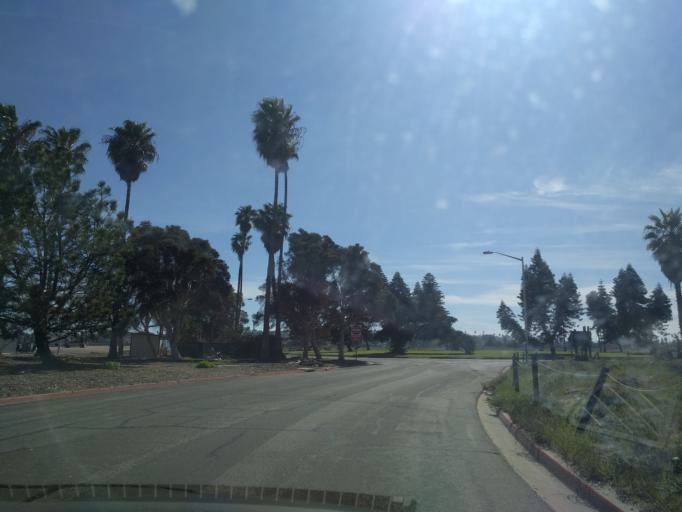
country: US
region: California
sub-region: San Diego County
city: La Jolla
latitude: 32.7596
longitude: -117.2411
